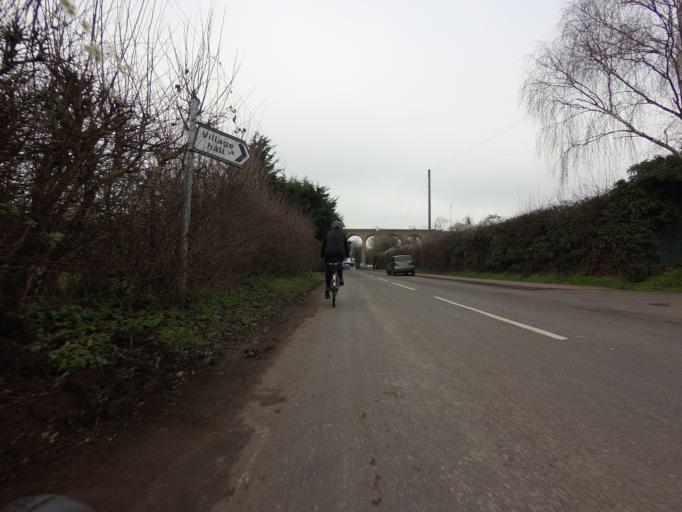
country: GB
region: England
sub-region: Kent
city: Eynsford
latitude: 51.3999
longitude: 0.2458
